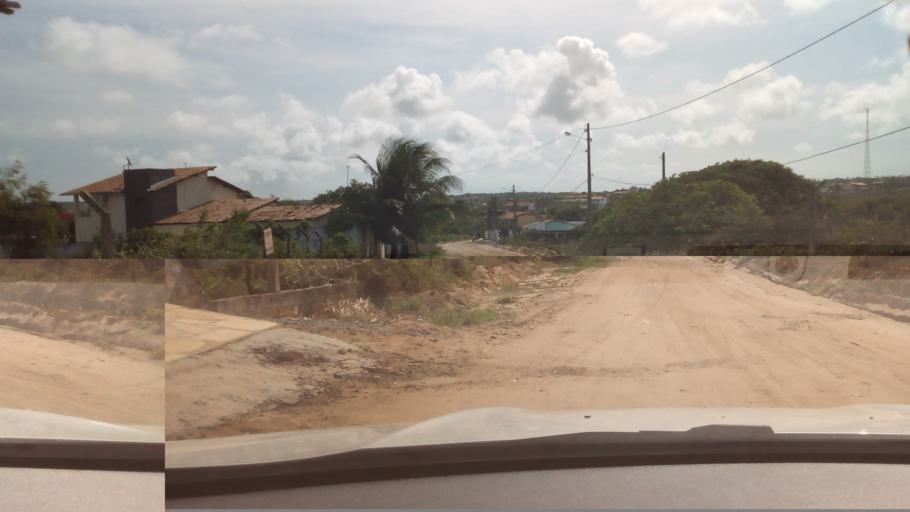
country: BR
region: Paraiba
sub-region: Conde
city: Conde
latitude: -7.3033
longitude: -34.8030
